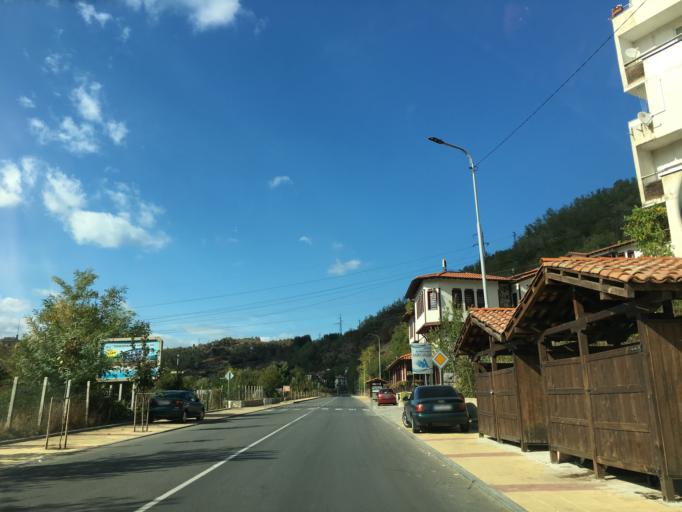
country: BG
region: Smolyan
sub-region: Obshtina Zlatograd
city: Zlatograd
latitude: 41.3877
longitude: 25.0880
